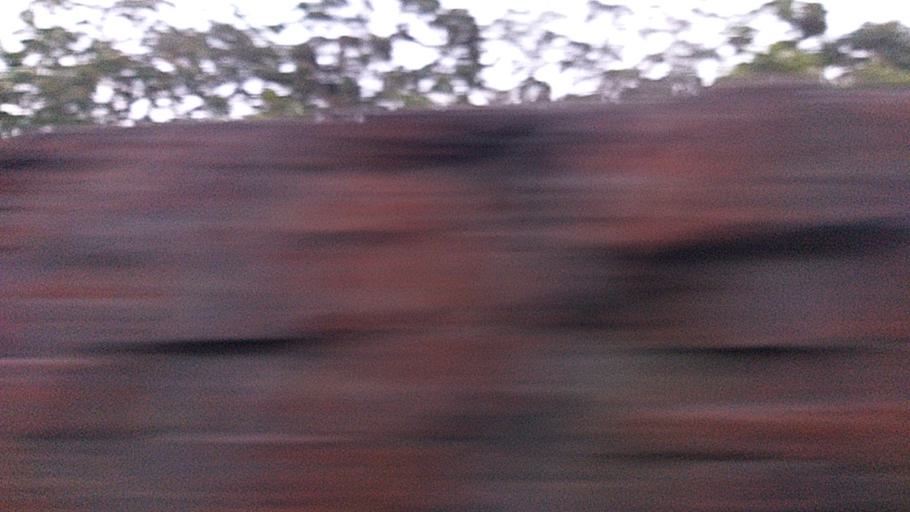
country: AU
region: New South Wales
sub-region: Wollongong
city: Helensburgh
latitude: -34.1618
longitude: 150.9993
